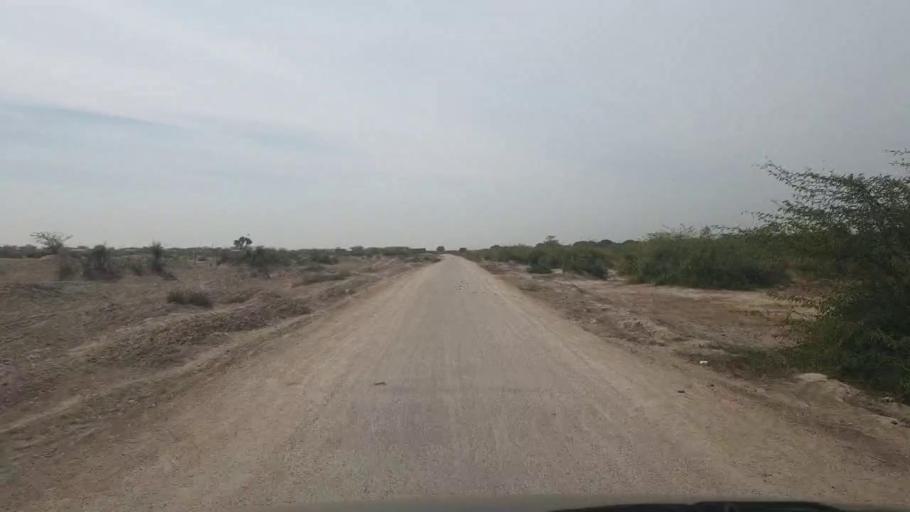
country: PK
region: Sindh
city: Umarkot
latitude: 25.2432
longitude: 69.7156
